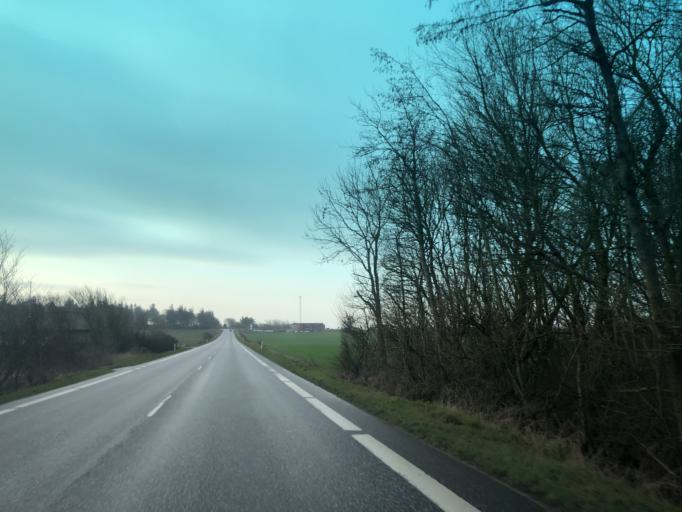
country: DK
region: North Denmark
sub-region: Thisted Kommune
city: Hurup
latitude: 56.7161
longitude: 8.4171
